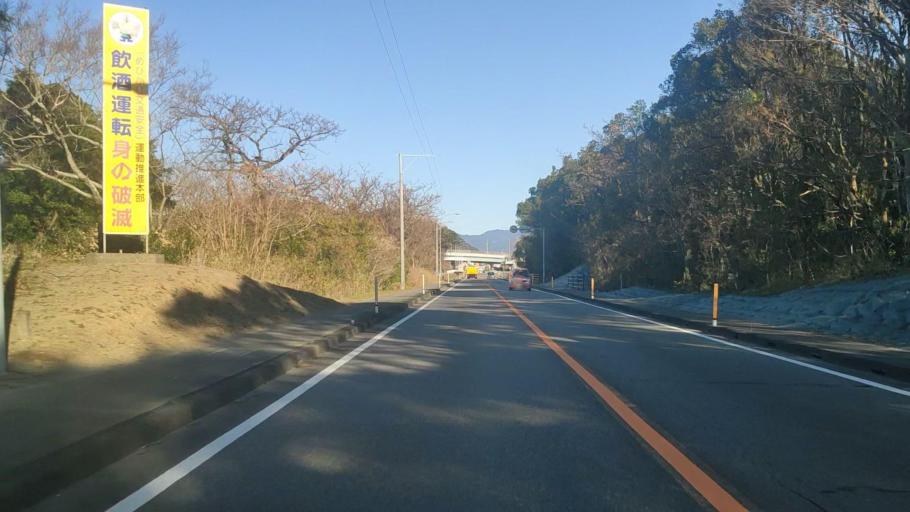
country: JP
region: Miyazaki
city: Nobeoka
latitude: 32.5336
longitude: 131.6803
